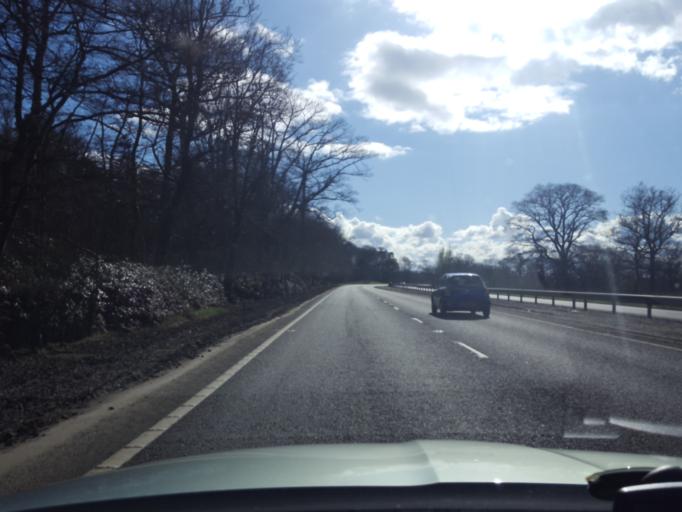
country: GB
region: Scotland
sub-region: Perth and Kinross
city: Errol
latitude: 56.4094
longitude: -3.2429
